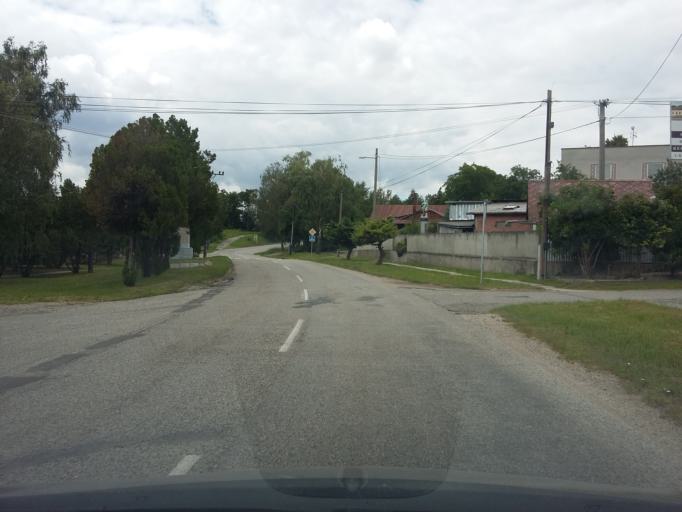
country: SK
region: Trnavsky
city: Smolenice
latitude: 48.5614
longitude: 17.3452
